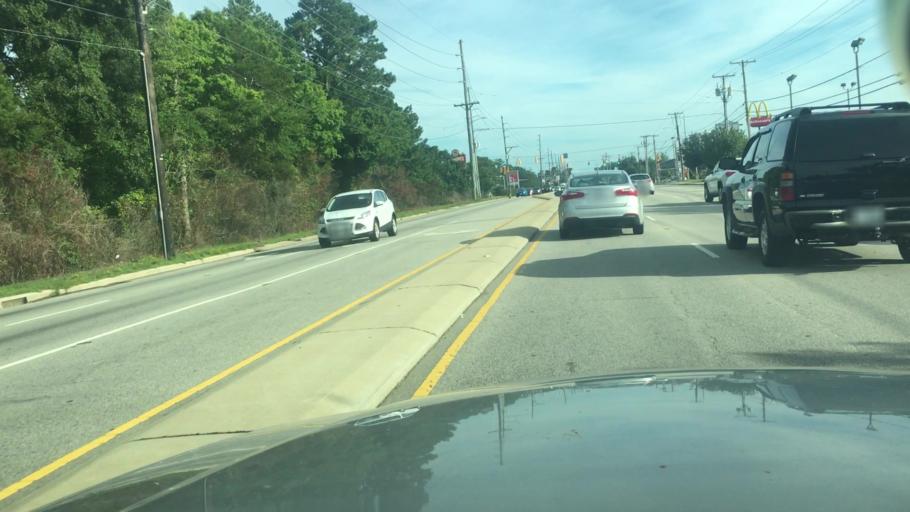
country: US
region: North Carolina
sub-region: Cumberland County
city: Fayetteville
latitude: 35.1141
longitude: -78.8798
